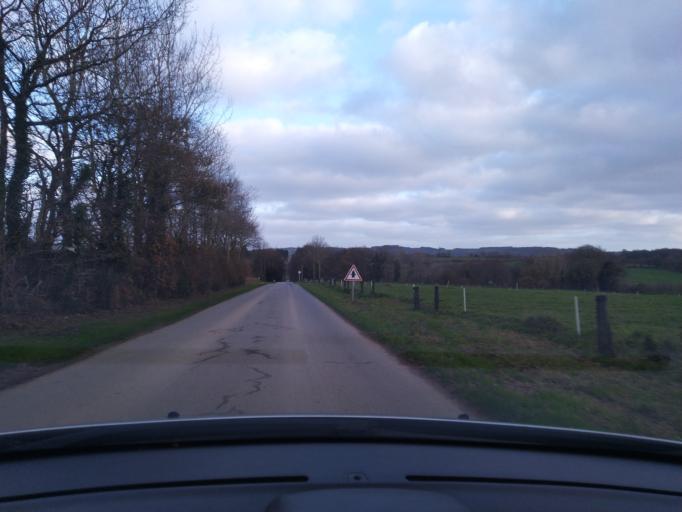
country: FR
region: Brittany
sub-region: Departement du Finistere
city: Plouigneau
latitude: 48.5669
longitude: -3.6662
